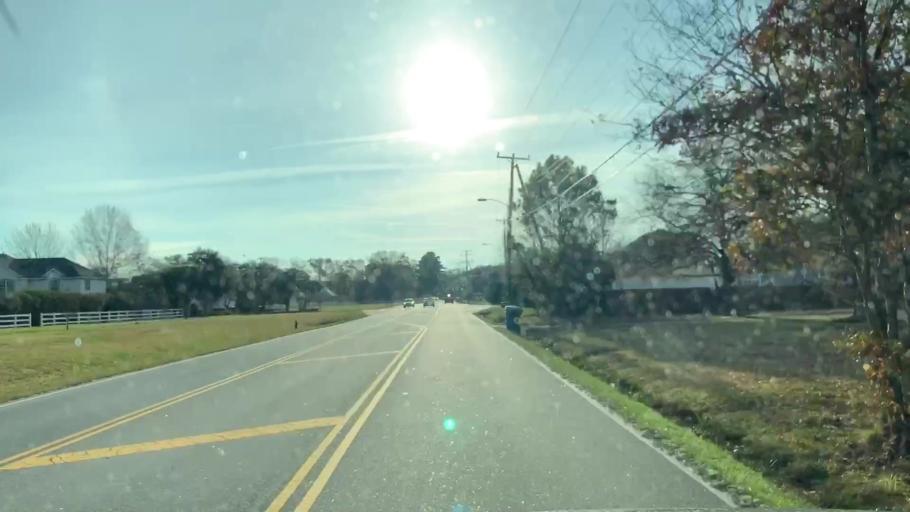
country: US
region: Virginia
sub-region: City of Chesapeake
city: Chesapeake
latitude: 36.7587
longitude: -76.1366
